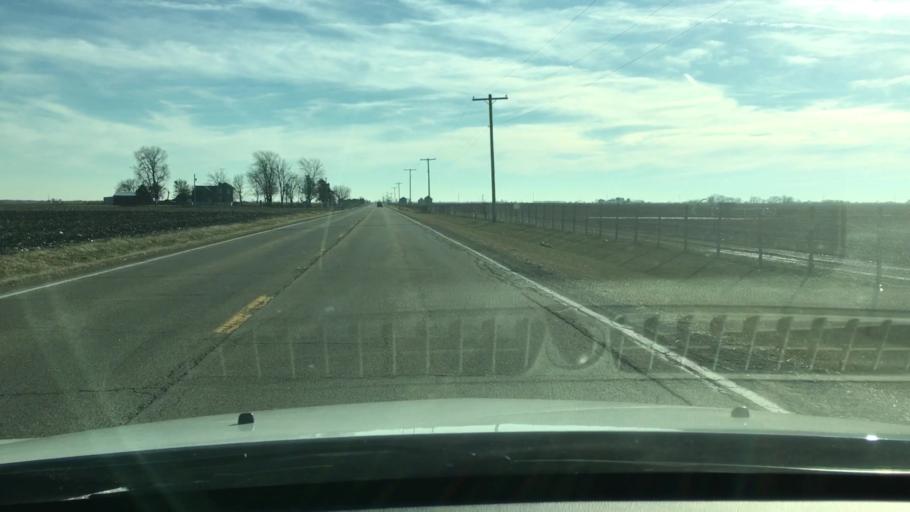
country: US
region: Illinois
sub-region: LaSalle County
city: Mendota
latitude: 41.4522
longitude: -89.1268
